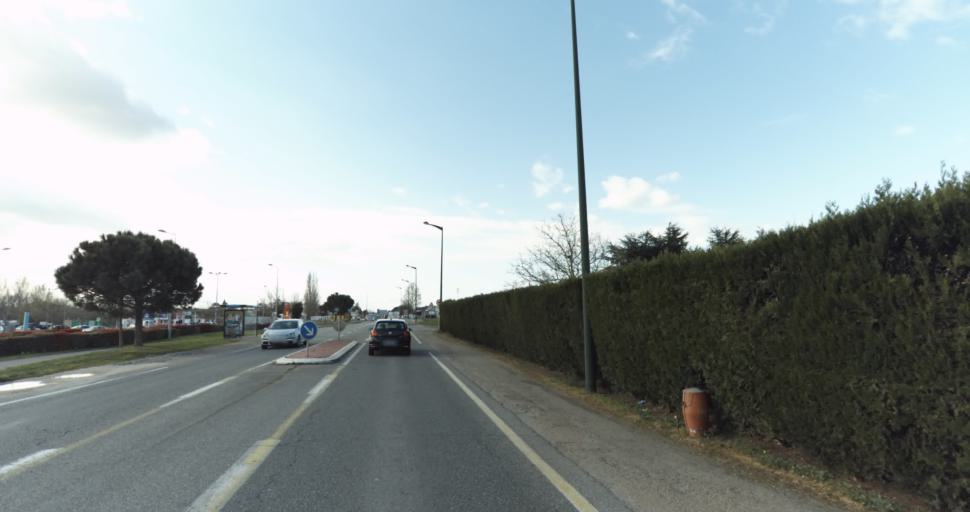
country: FR
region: Midi-Pyrenees
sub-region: Departement de la Haute-Garonne
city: Auterive
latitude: 43.3628
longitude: 1.4595
